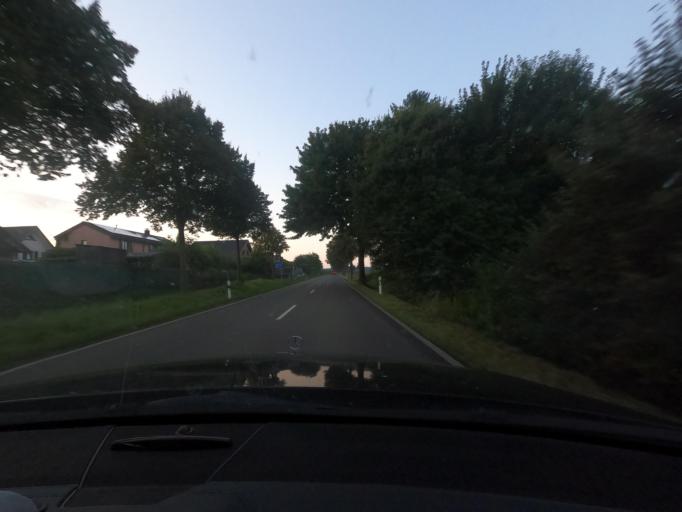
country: DE
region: North Rhine-Westphalia
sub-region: Regierungsbezirk Detmold
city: Salzkotten
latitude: 51.6574
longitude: 8.5920
